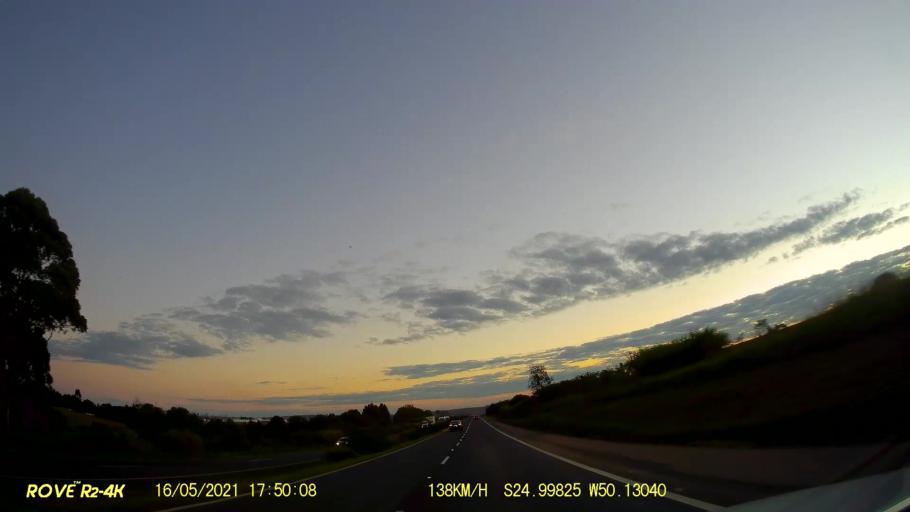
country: BR
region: Parana
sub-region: Carambei
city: Carambei
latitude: -24.9983
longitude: -50.1303
